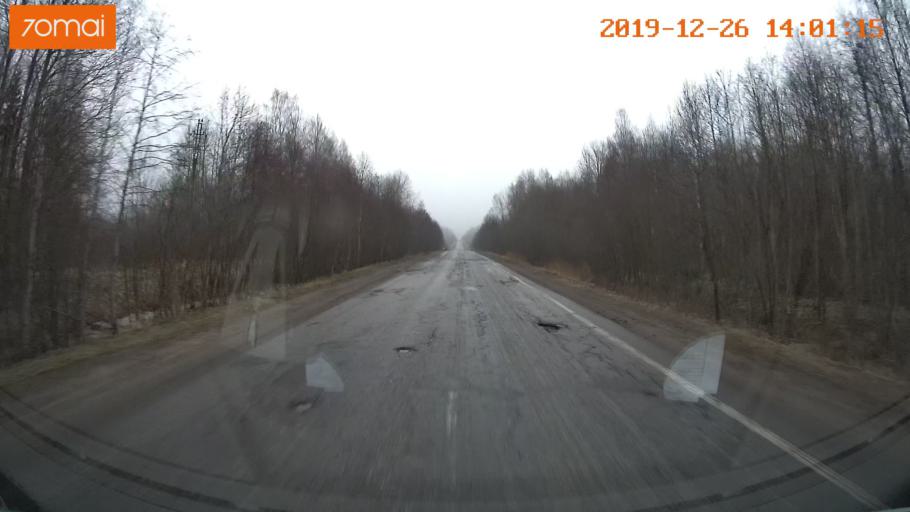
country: RU
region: Jaroslavl
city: Poshekhon'ye
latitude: 58.5518
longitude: 38.7602
